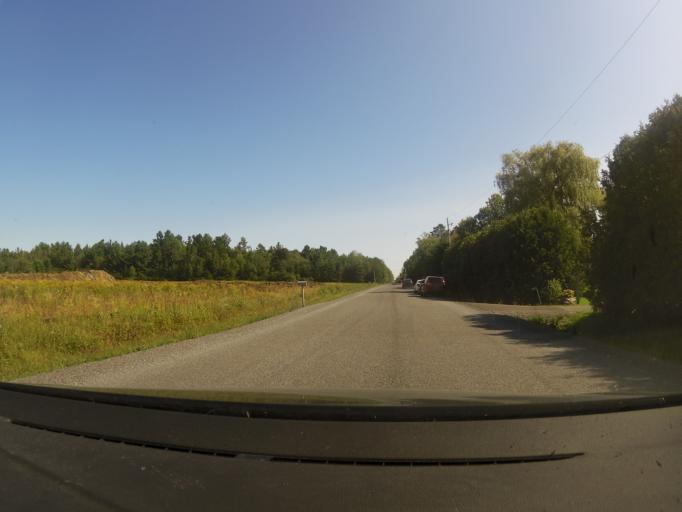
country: CA
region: Ontario
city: Carleton Place
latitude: 45.3133
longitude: -76.0438
